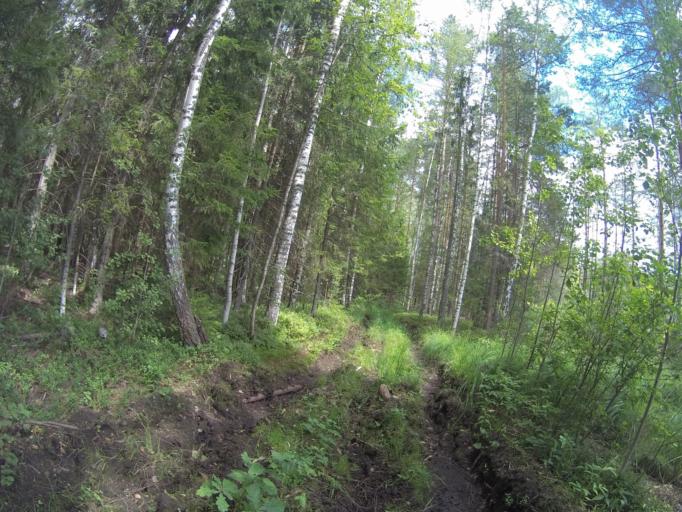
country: RU
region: Vladimir
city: Kommunar
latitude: 56.0551
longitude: 40.5177
